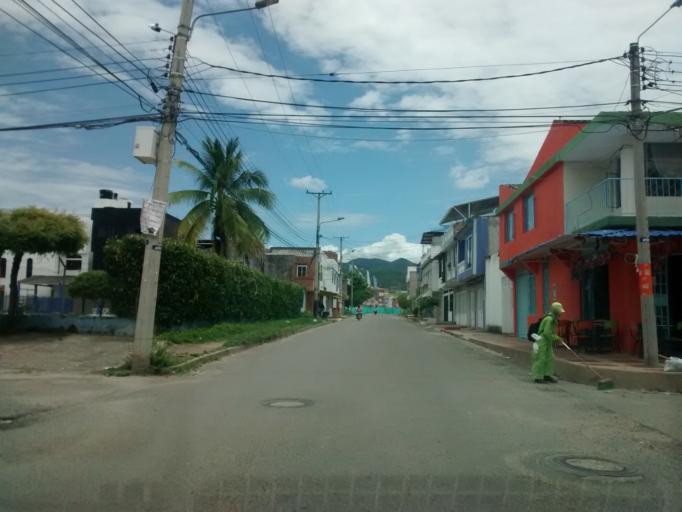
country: CO
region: Cundinamarca
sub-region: Girardot
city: Girardot City
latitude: 4.3095
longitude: -74.8068
